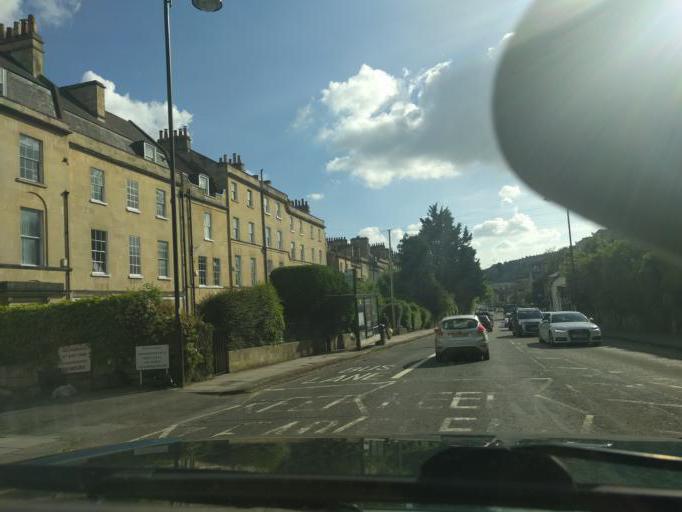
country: GB
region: England
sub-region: Bath and North East Somerset
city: Bath
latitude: 51.3937
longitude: -2.3477
